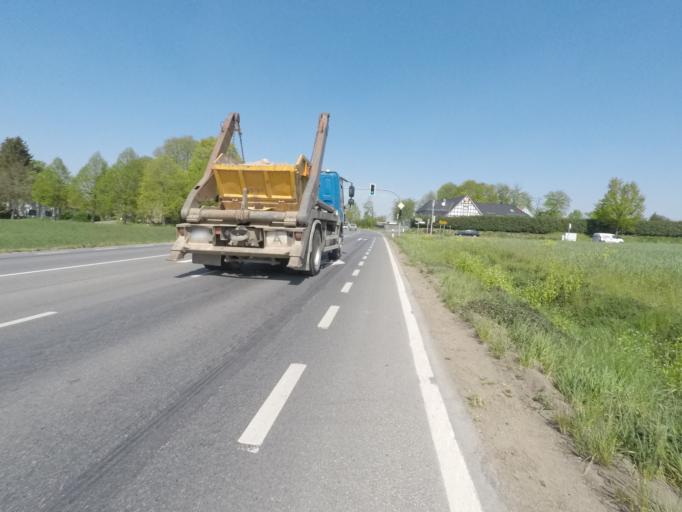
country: DE
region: North Rhine-Westphalia
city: Enger
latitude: 52.0909
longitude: 8.5861
